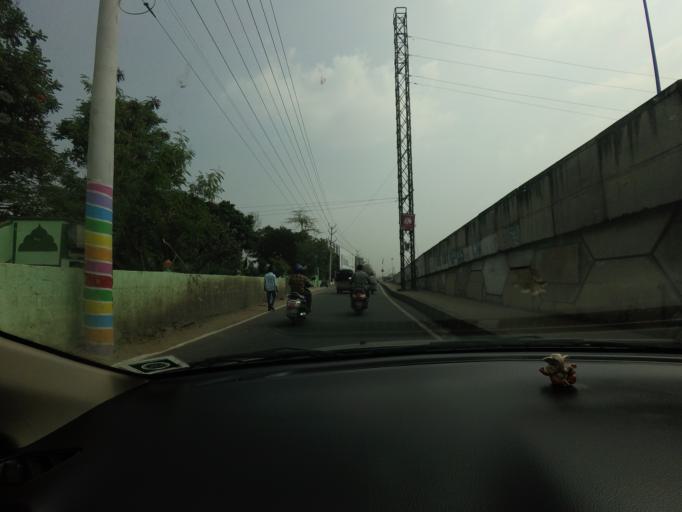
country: IN
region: Andhra Pradesh
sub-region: Krishna
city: Vijayawada
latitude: 16.5008
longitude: 80.6359
